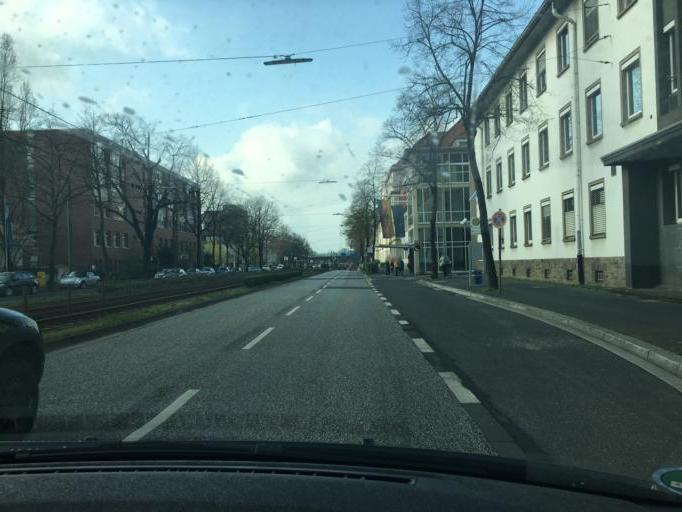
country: DE
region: North Rhine-Westphalia
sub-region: Regierungsbezirk Koln
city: Bonn
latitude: 50.7500
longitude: 7.0921
